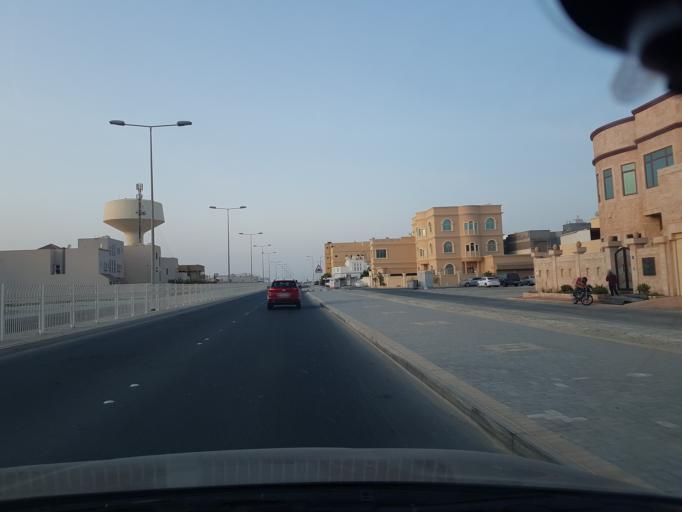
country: BH
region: Muharraq
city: Al Hadd
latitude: 26.2784
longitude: 50.6421
